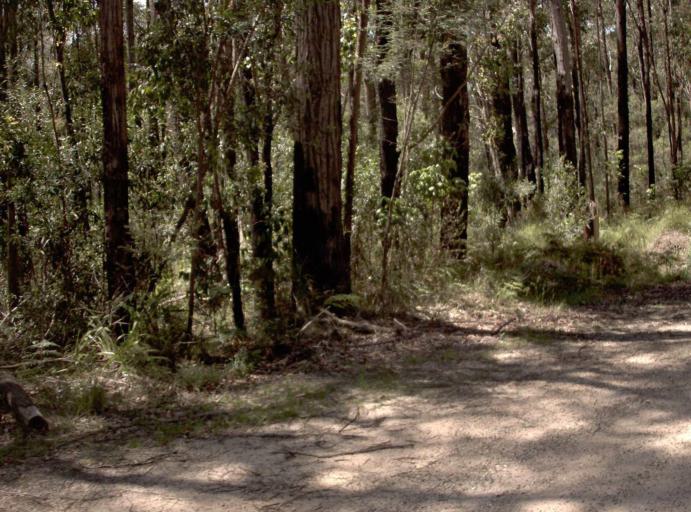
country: AU
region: New South Wales
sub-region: Bombala
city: Bombala
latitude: -37.5763
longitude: 149.0186
